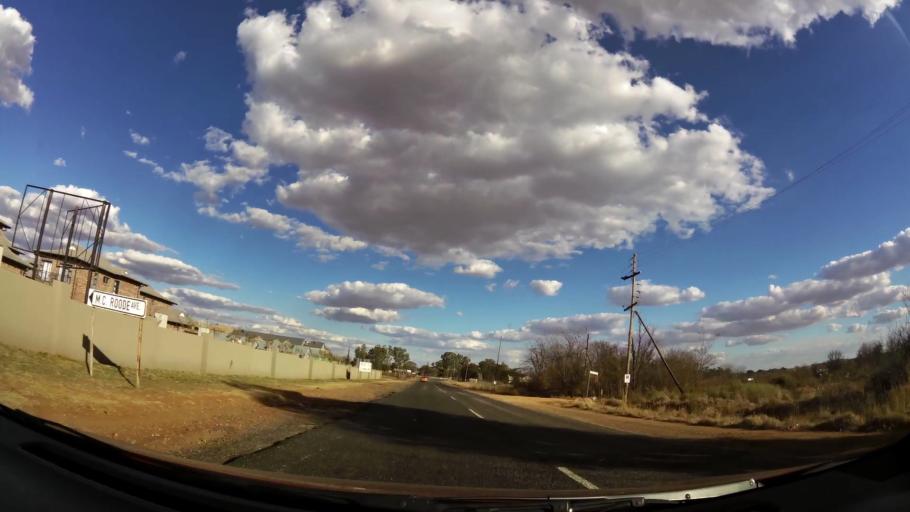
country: ZA
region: North-West
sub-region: Dr Kenneth Kaunda District Municipality
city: Potchefstroom
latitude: -26.6692
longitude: 27.1058
